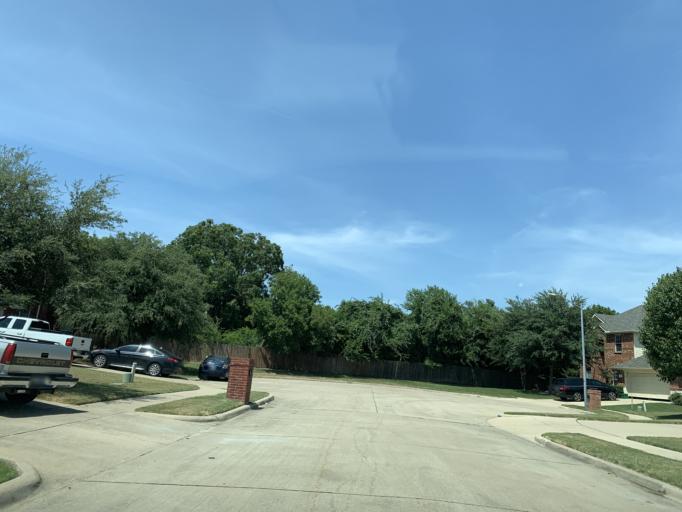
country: US
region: Texas
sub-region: Dallas County
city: Cedar Hill
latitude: 32.6462
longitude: -97.0179
